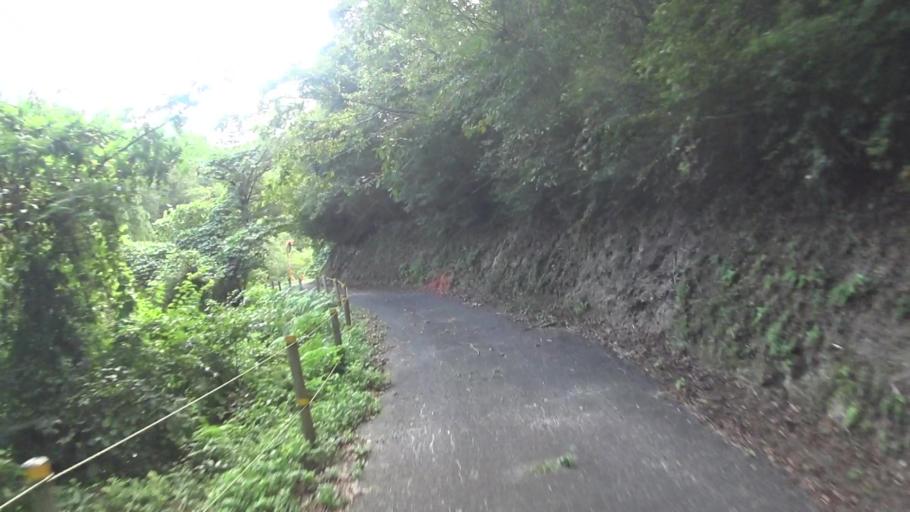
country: JP
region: Kyoto
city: Miyazu
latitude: 35.6695
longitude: 135.1406
